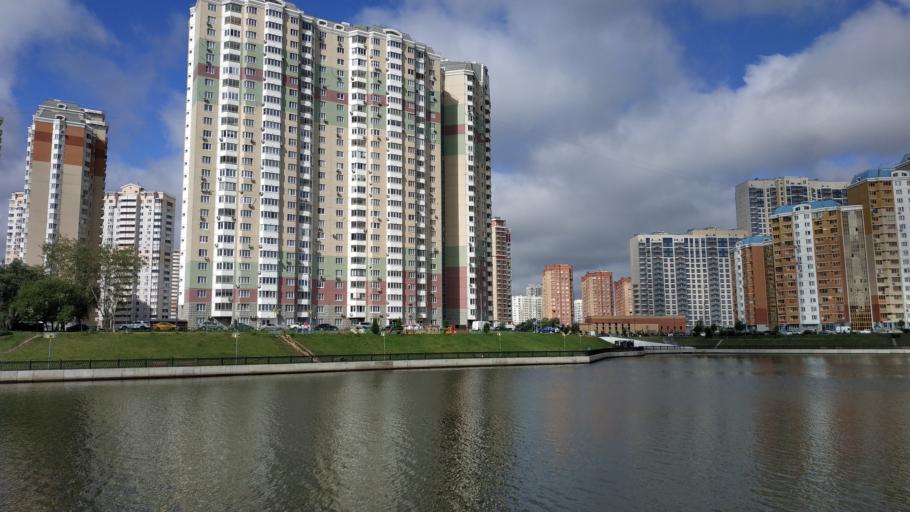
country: RU
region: Moskovskaya
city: Pavshino
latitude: 55.8241
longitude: 37.3804
